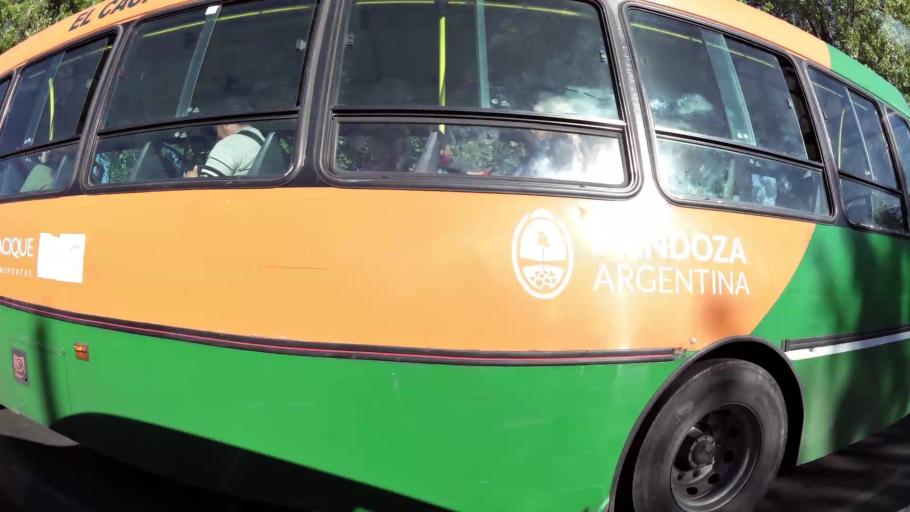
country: AR
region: Mendoza
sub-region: Departamento de Godoy Cruz
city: Godoy Cruz
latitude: -32.9313
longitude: -68.8392
